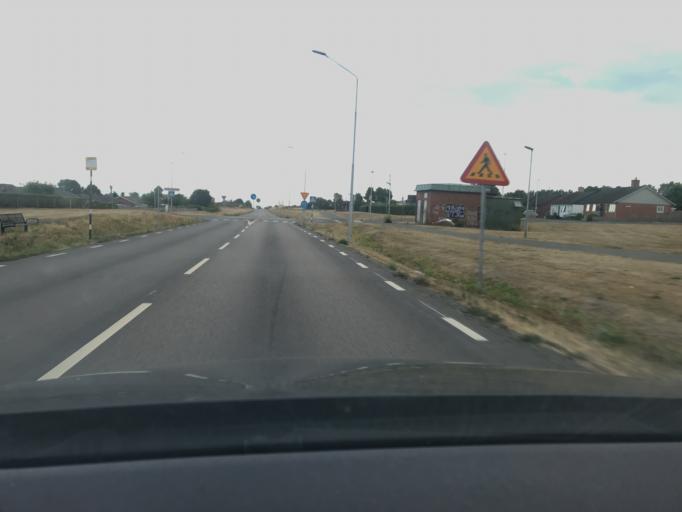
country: SE
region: Skane
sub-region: Simrishamns Kommun
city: Simrishamn
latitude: 55.5463
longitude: 14.3513
